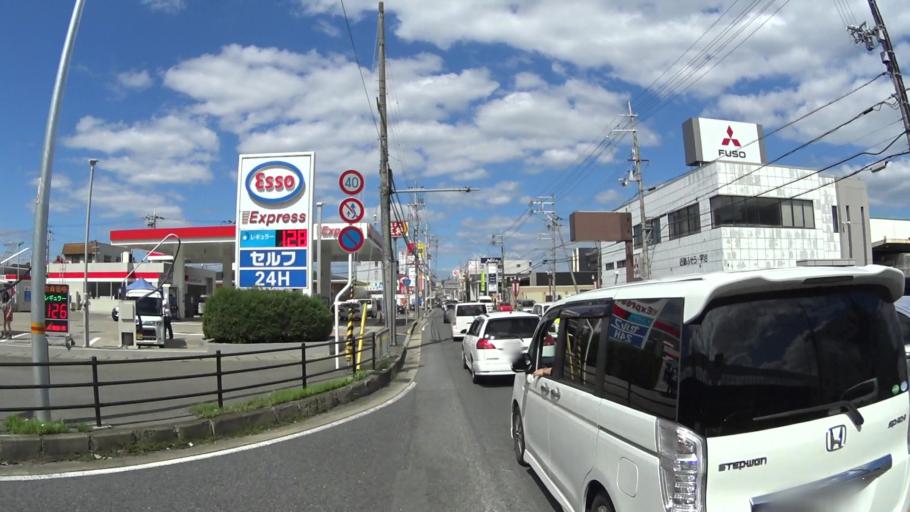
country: JP
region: Kyoto
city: Uji
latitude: 34.9087
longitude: 135.7838
